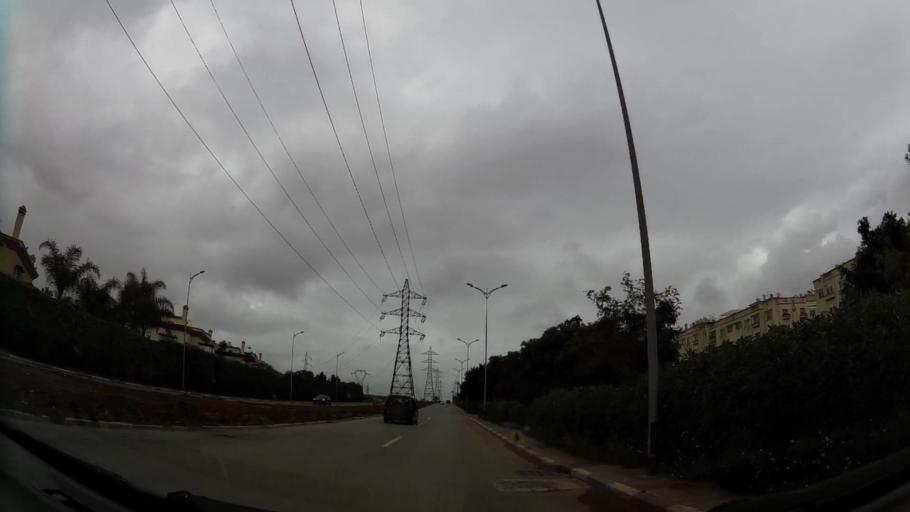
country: MA
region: Grand Casablanca
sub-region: Casablanca
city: Casablanca
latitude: 33.5266
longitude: -7.6169
